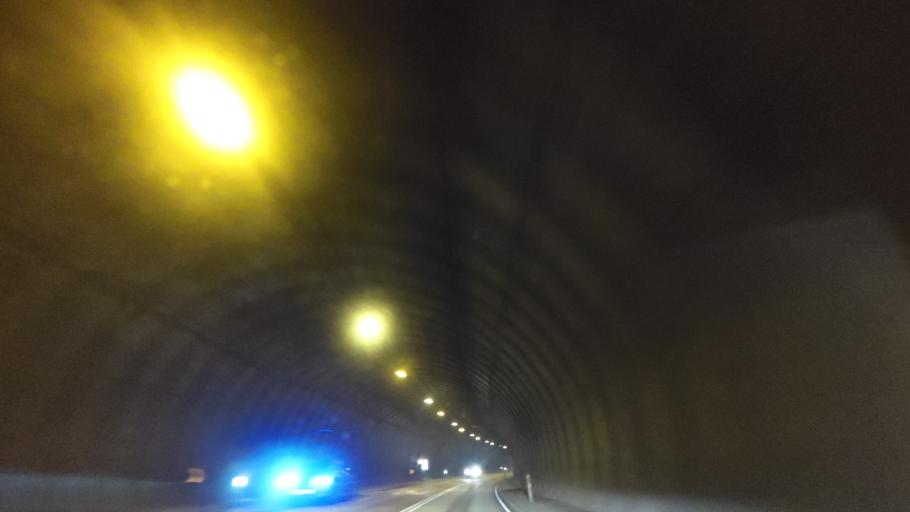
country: IS
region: West
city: Akranes
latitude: 64.3135
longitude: -21.9020
